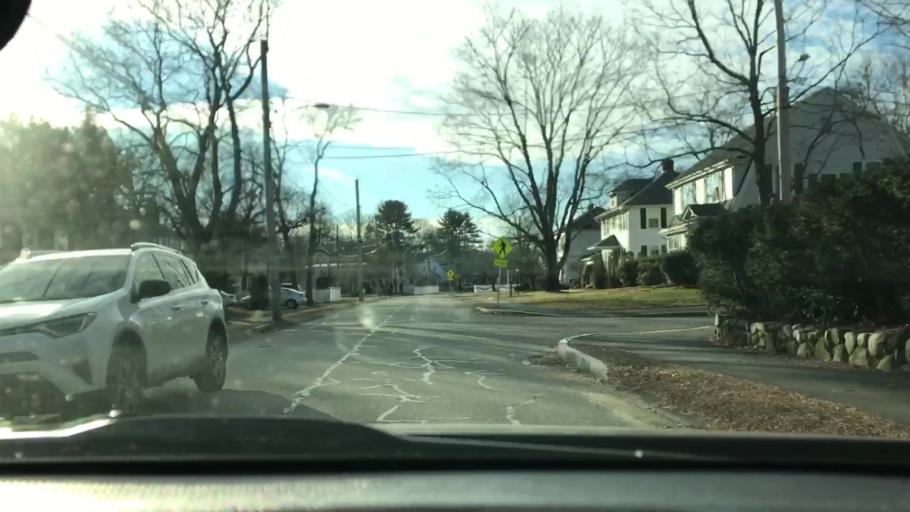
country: US
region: Massachusetts
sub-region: Norfolk County
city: Needham
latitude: 42.2893
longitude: -71.2284
